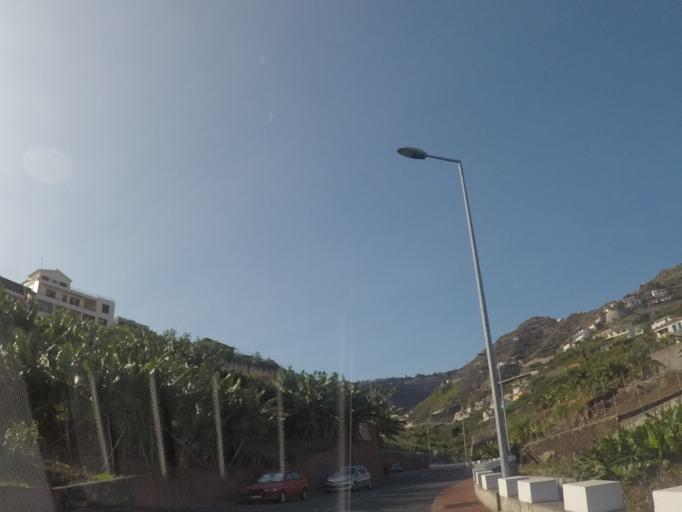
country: PT
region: Madeira
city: Camara de Lobos
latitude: 32.6538
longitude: -16.9856
